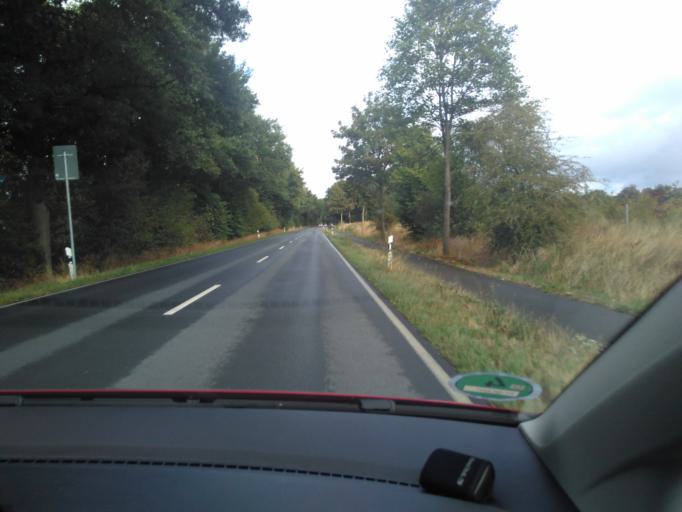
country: DE
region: North Rhine-Westphalia
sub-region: Regierungsbezirk Munster
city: Warendorf
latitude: 51.9716
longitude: 7.9626
